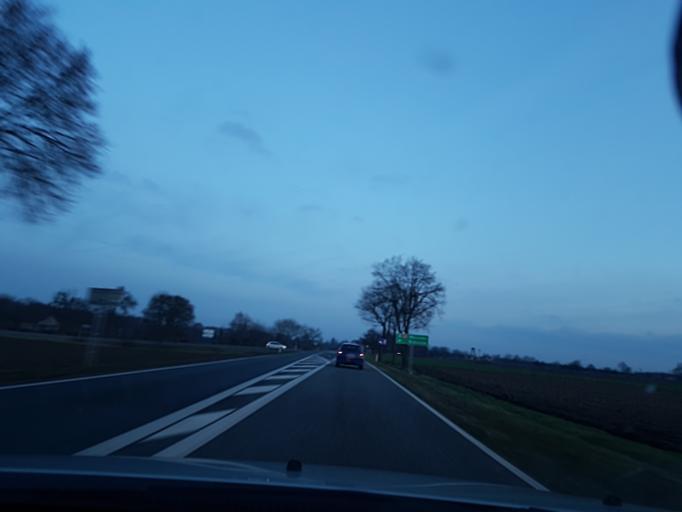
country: PL
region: Masovian Voivodeship
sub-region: Powiat plocki
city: Mala Wies
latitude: 52.4104
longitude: 20.1293
